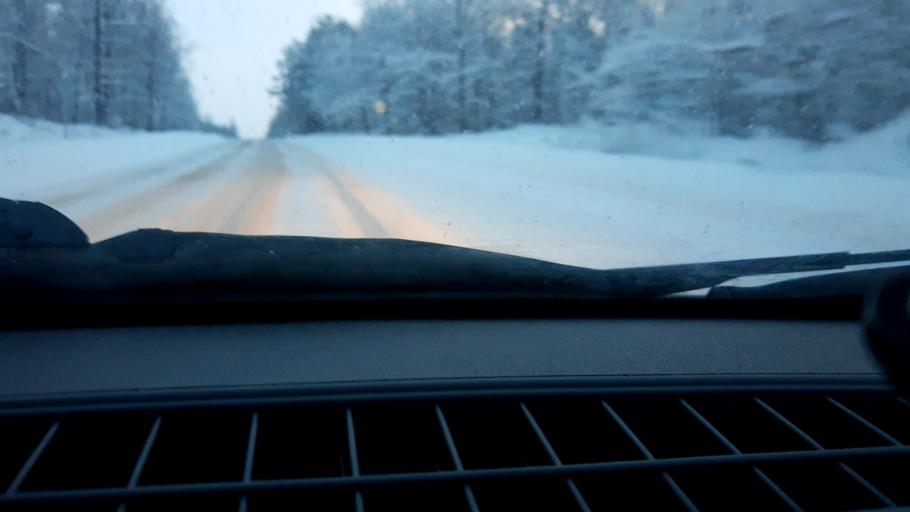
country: RU
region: Bashkortostan
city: Davlekanovo
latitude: 54.5668
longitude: 54.9659
